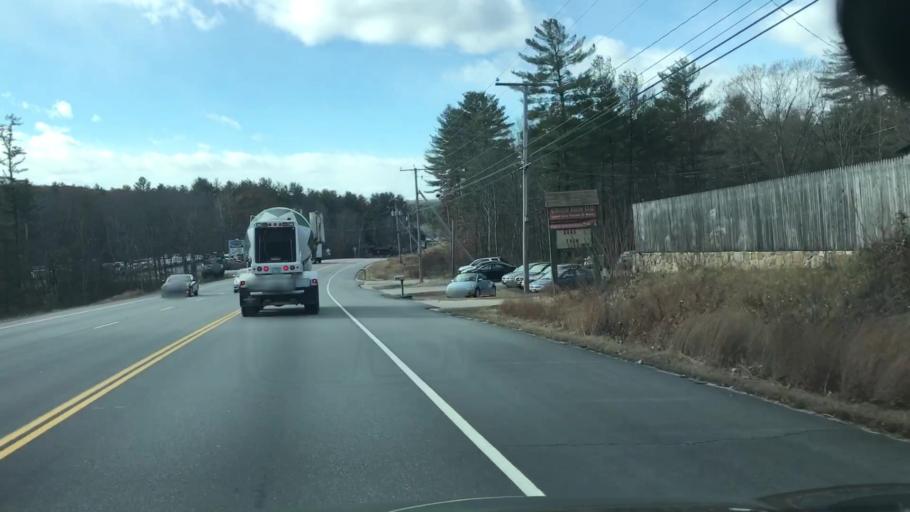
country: US
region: New Hampshire
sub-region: Merrimack County
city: Chichester
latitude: 43.2450
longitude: -71.4387
